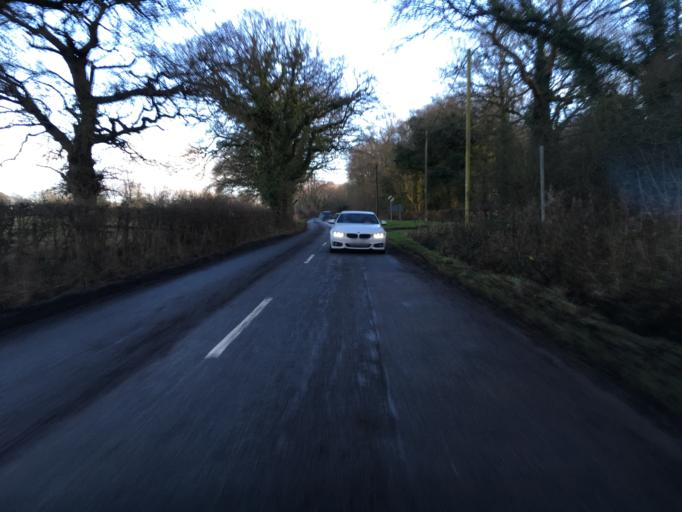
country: GB
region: England
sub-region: Warwickshire
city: Stratford-upon-Avon
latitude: 52.2435
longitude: -1.7276
